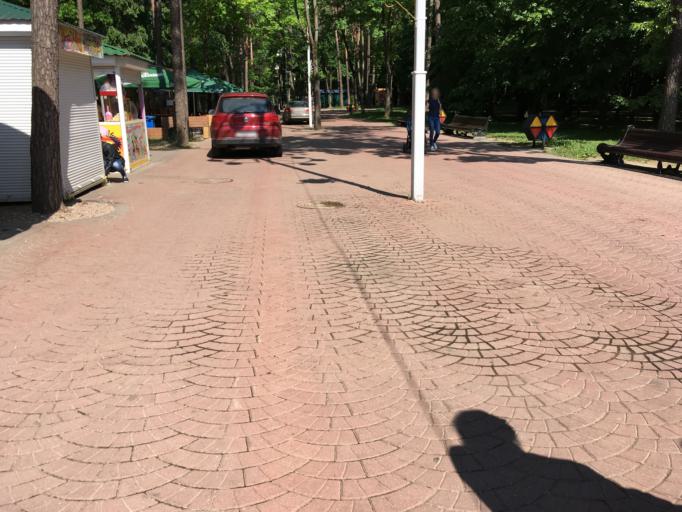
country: BY
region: Minsk
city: Minsk
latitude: 53.9203
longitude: 27.6143
